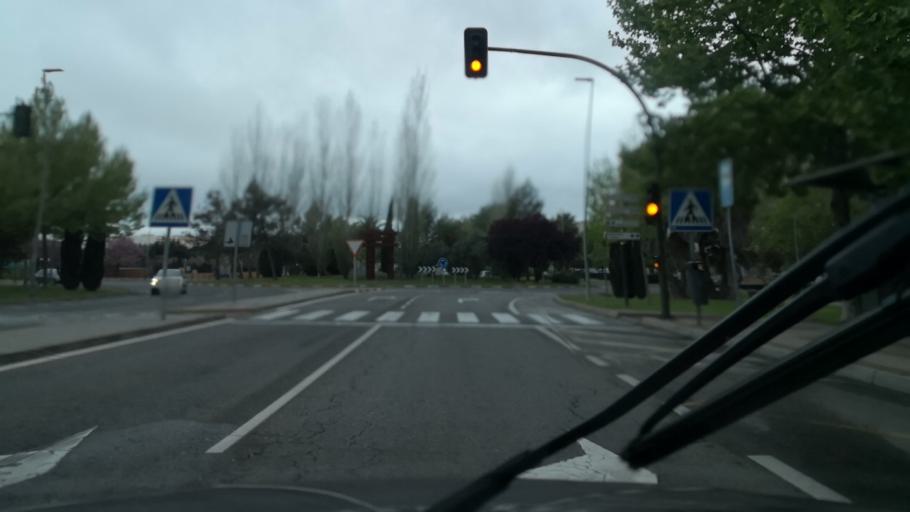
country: ES
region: Extremadura
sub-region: Provincia de Caceres
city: Caceres
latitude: 39.4703
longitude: -6.3911
